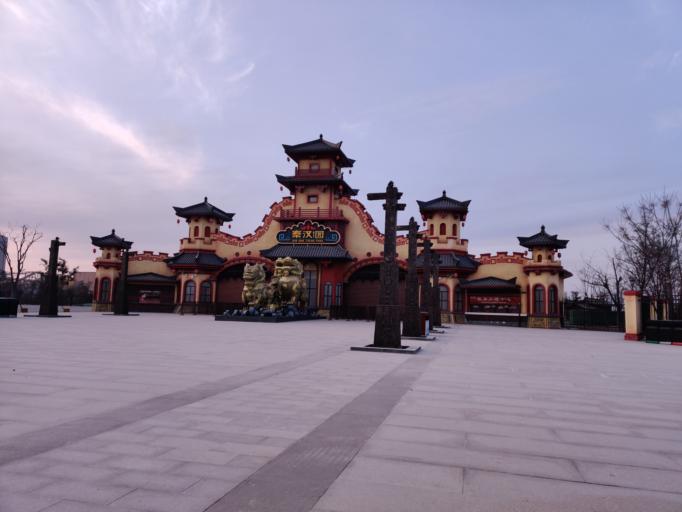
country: CN
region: Shaanxi
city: Gaozhuang
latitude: 34.4763
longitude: 108.9169
